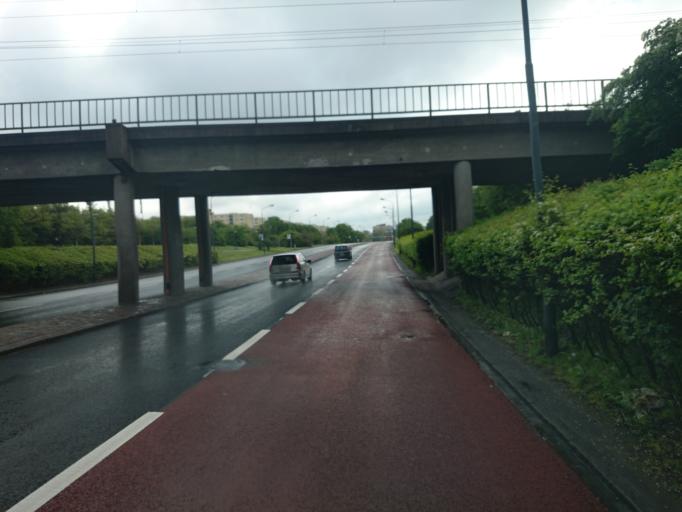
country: SE
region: Skane
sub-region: Malmo
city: Malmoe
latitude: 55.5899
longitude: 13.0309
